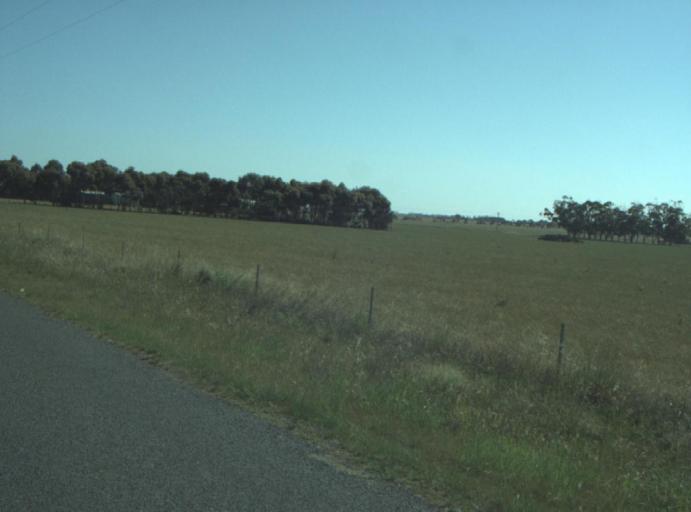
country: AU
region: Victoria
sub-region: Wyndham
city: Little River
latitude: -37.9602
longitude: 144.4634
